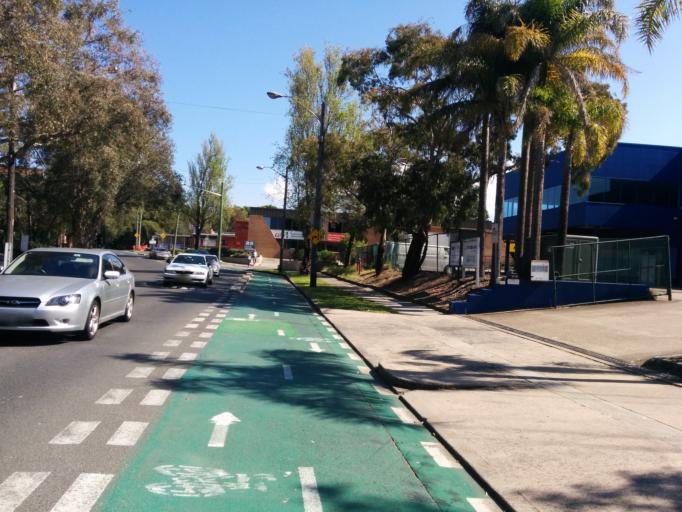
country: AU
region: New South Wales
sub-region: City of Sydney
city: Alexandria
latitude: -33.9071
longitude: 151.1981
